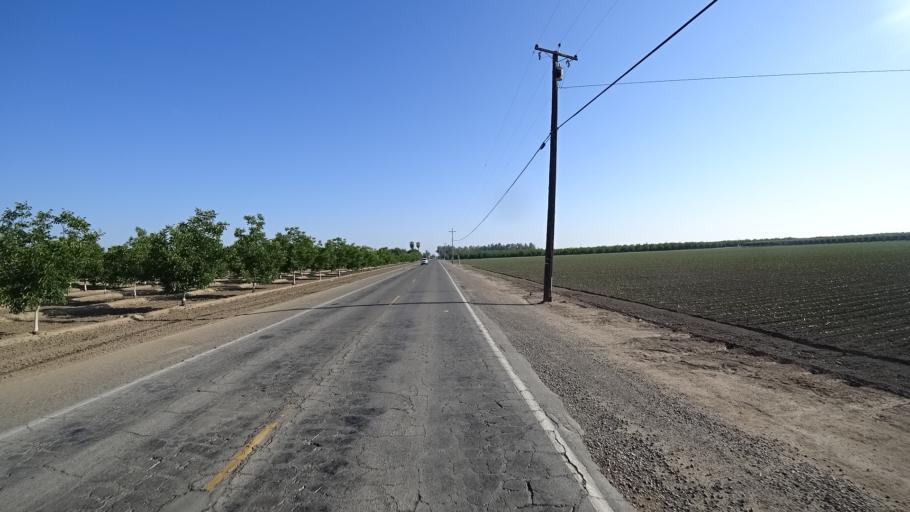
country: US
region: California
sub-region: Kings County
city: Armona
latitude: 36.2591
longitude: -119.7090
